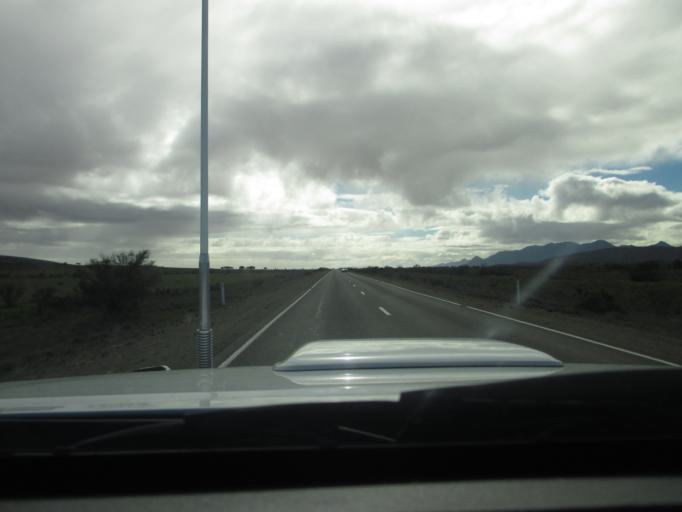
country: AU
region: South Australia
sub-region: Flinders Ranges
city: Quorn
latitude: -31.6371
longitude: 138.3859
